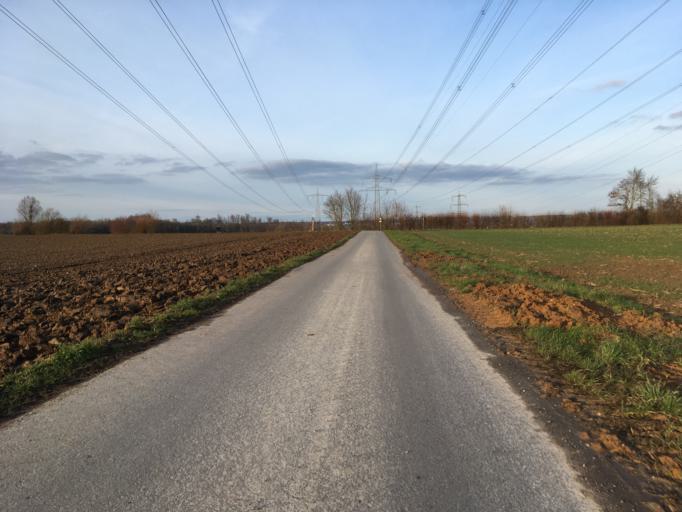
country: DE
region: Baden-Wuerttemberg
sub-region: Regierungsbezirk Stuttgart
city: Bad Wimpfen
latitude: 49.2265
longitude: 9.1329
